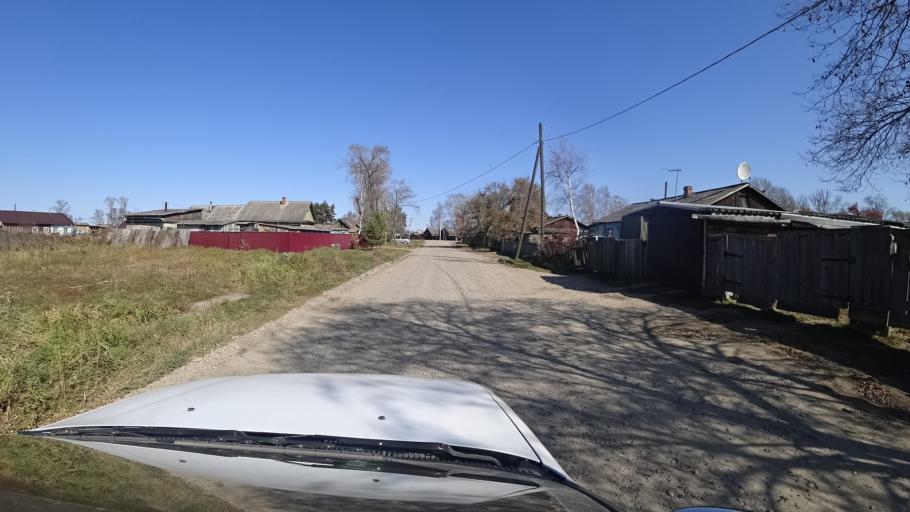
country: RU
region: Primorskiy
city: Dal'nerechensk
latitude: 45.9261
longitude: 133.7511
